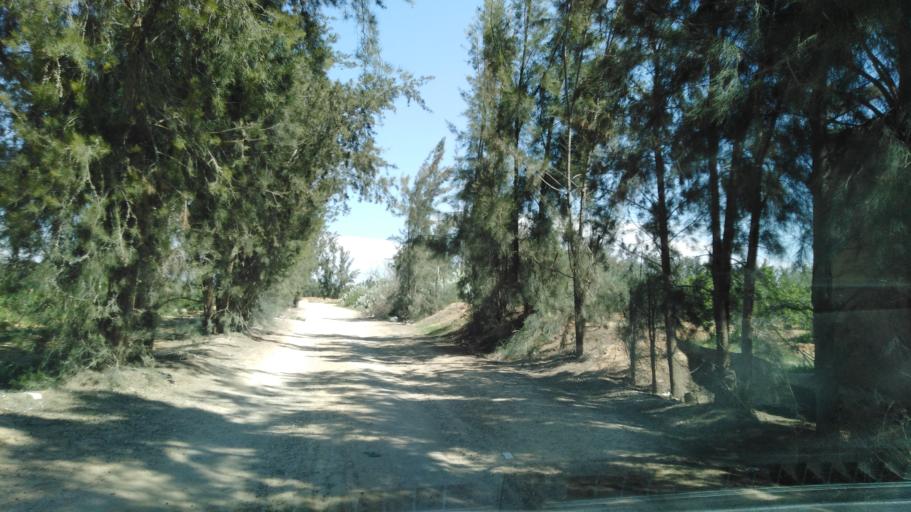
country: TN
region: Safaqis
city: Sfax
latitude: 34.7639
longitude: 10.5284
